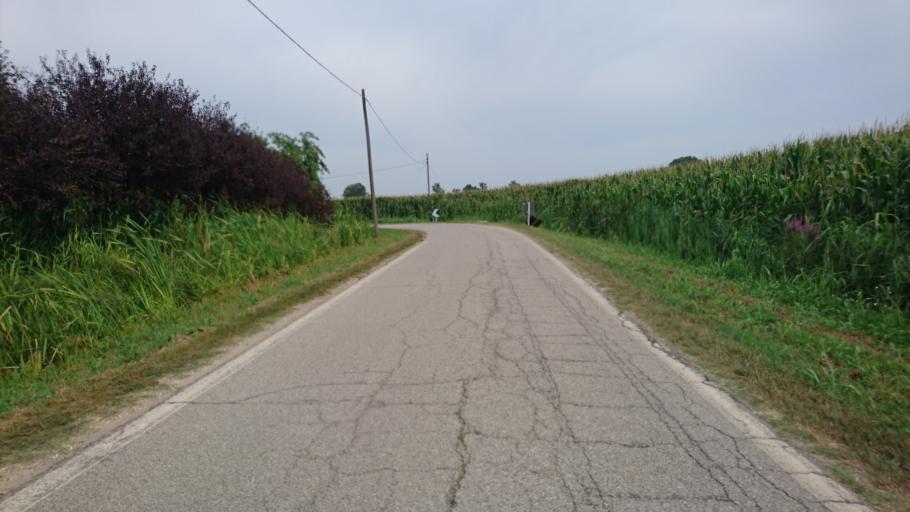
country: IT
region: Veneto
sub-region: Provincia di Venezia
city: Sant'Anna
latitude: 45.1431
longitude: 12.2753
